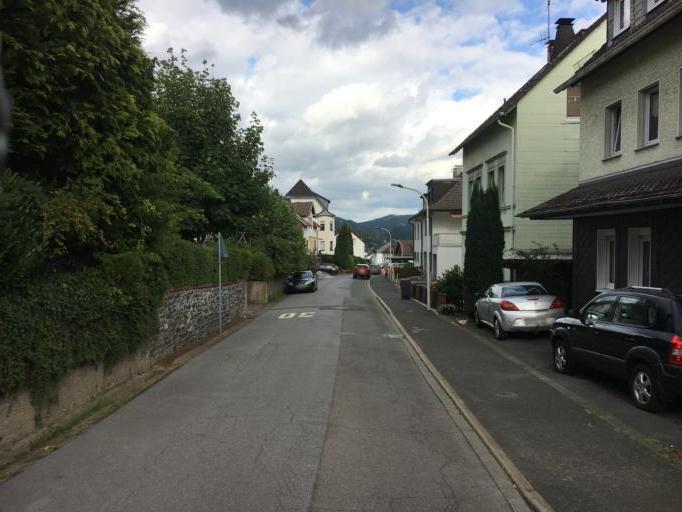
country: DE
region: North Rhine-Westphalia
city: Plettenberg
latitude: 51.2010
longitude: 7.8476
